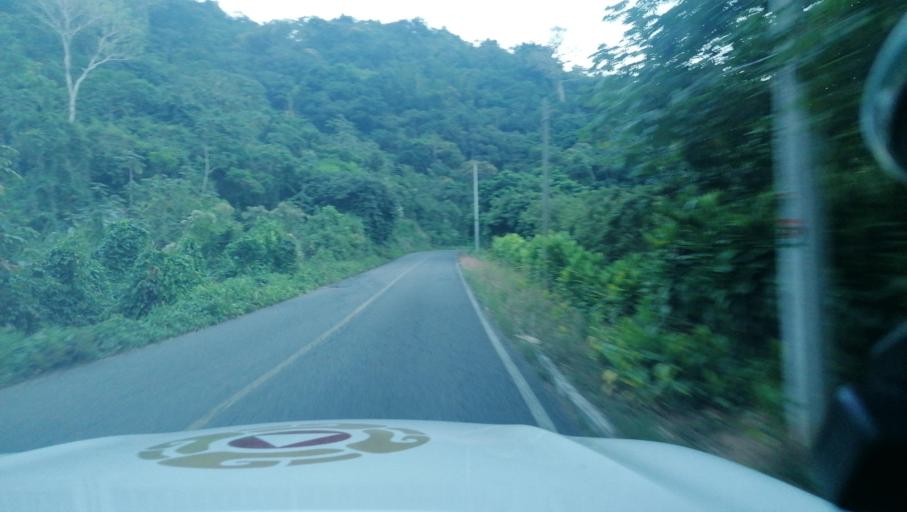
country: MX
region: Chiapas
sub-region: Cacahoatan
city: Benito Juarez
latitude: 15.0424
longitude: -92.2438
